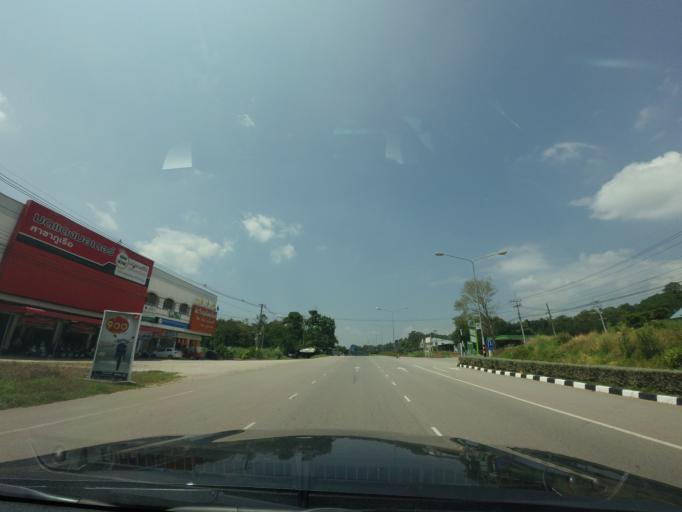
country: TH
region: Loei
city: Phu Ruea
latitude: 17.4568
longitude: 101.3703
